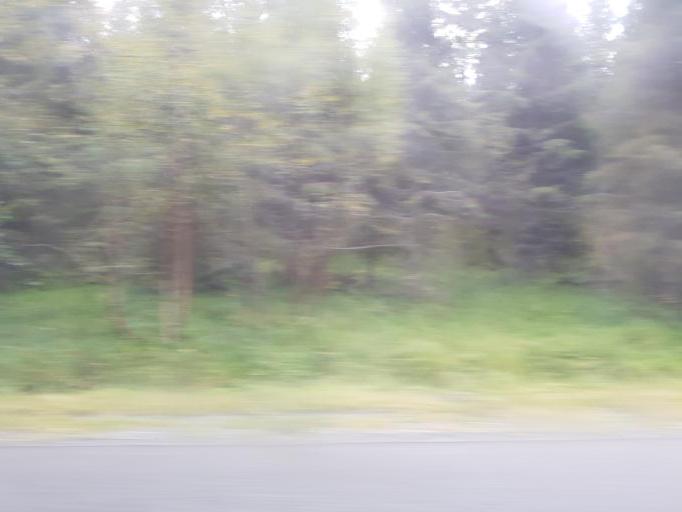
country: NO
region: Sor-Trondelag
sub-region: Trondheim
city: Trondheim
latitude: 63.4157
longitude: 10.3098
